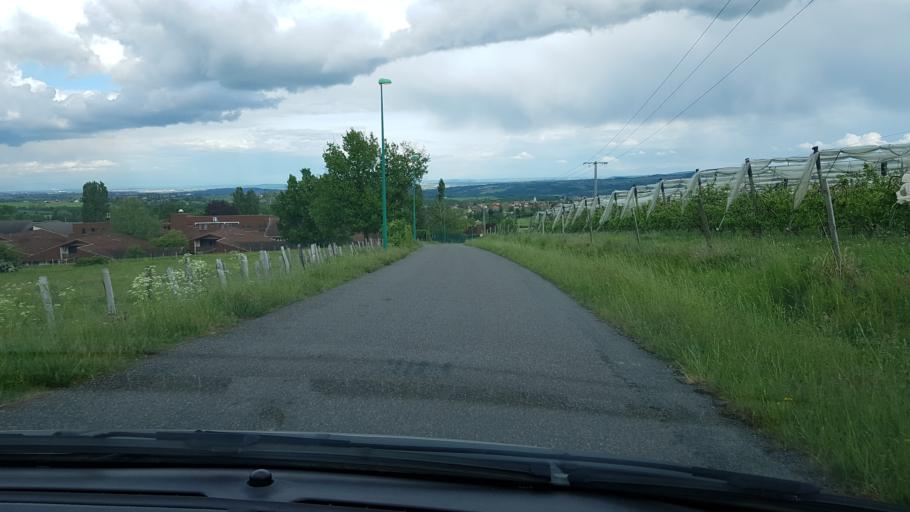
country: FR
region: Rhone-Alpes
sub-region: Departement du Rhone
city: Saint-Maurice-sur-Dargoire
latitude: 45.5797
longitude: 4.6389
